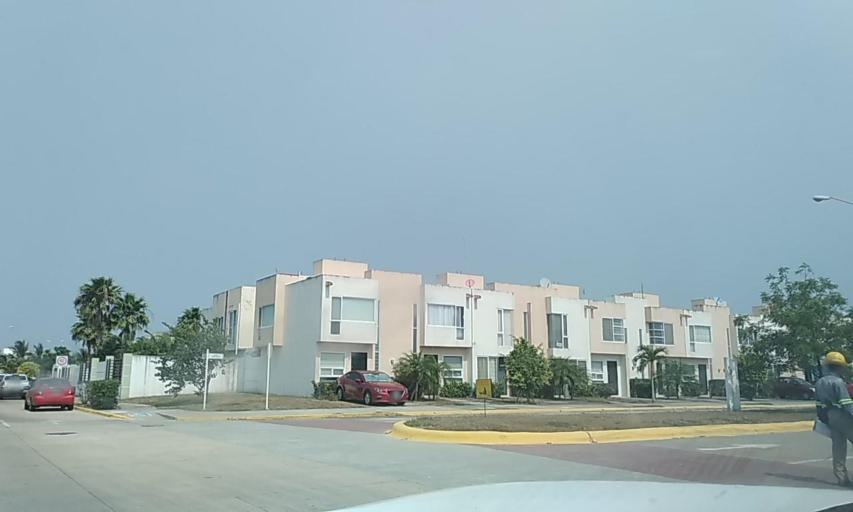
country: MX
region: Veracruz
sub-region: Veracruz
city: Hacienda Sotavento
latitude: 19.1328
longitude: -96.1691
